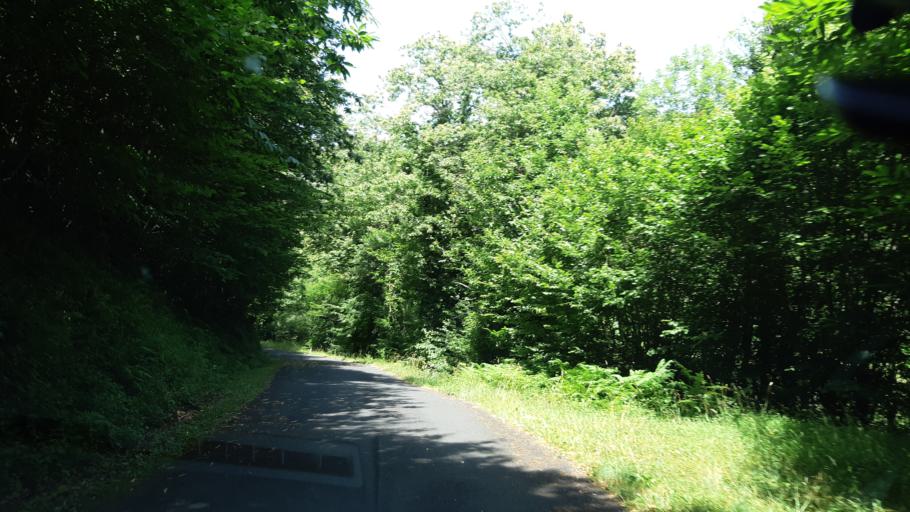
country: FR
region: Languedoc-Roussillon
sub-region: Departement des Pyrenees-Orientales
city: Arles
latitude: 42.5349
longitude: 2.5867
